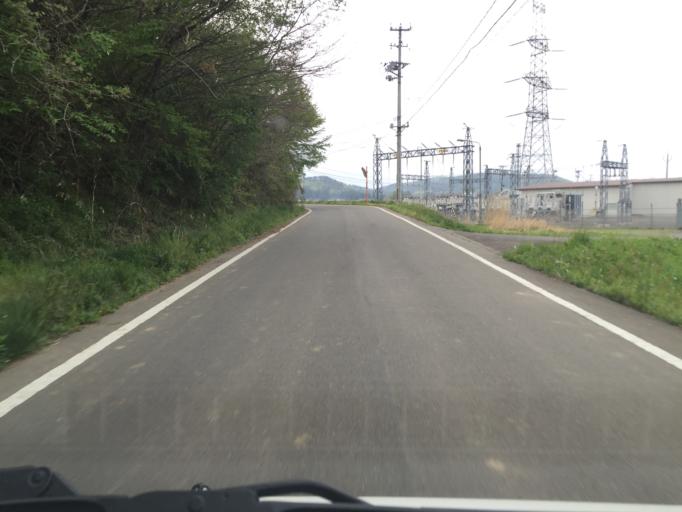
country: JP
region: Fukushima
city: Nihommatsu
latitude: 37.6458
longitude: 140.4519
